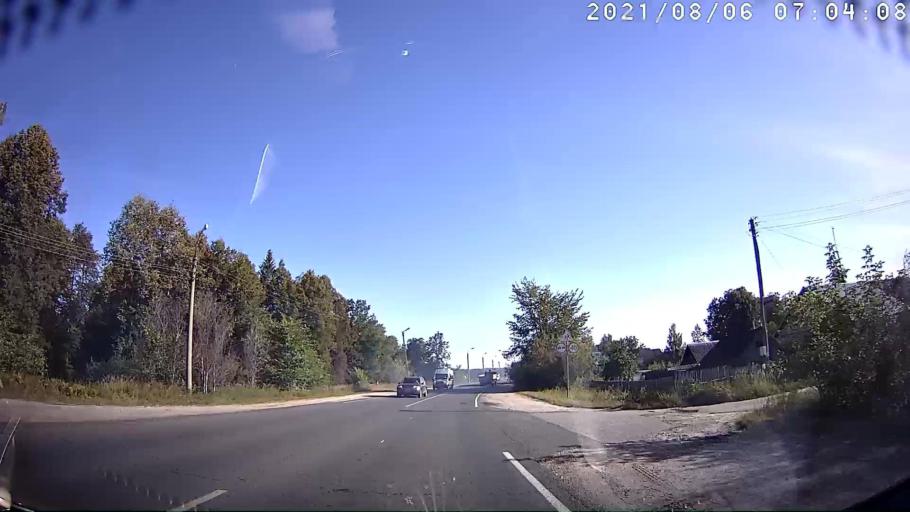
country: RU
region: Mariy-El
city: Yoshkar-Ola
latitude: 56.5446
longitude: 47.9809
